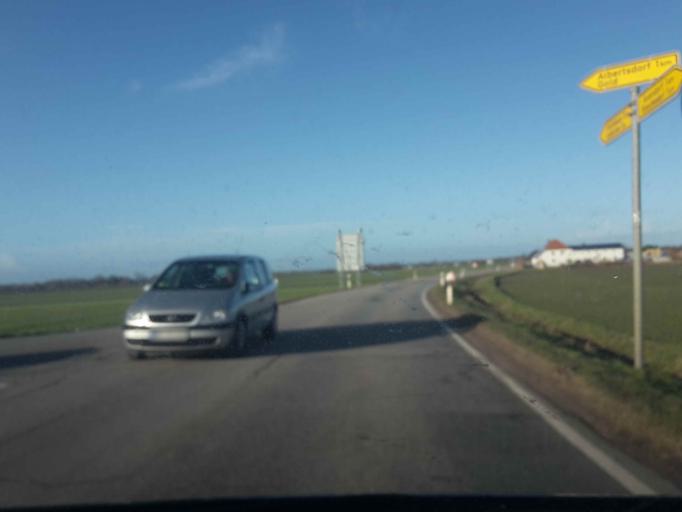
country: DE
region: Schleswig-Holstein
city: Fehmarn
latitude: 54.4280
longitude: 11.1334
